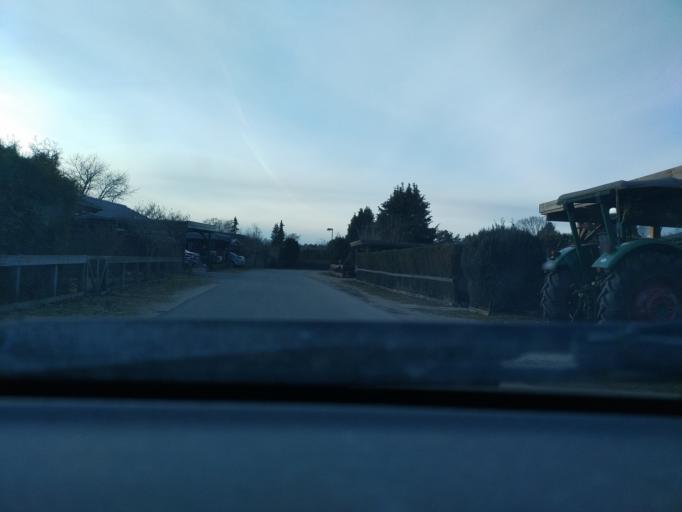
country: DE
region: Schleswig-Holstein
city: Fitzen
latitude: 53.5094
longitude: 10.6505
